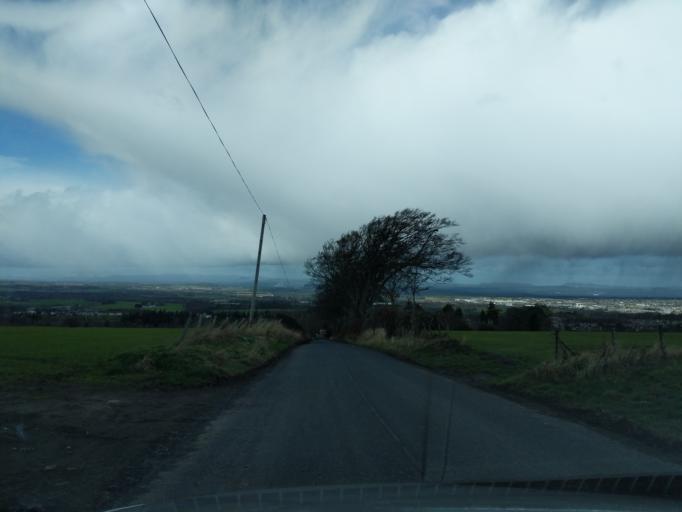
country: GB
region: Scotland
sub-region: Edinburgh
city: Currie
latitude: 55.8888
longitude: -3.3027
